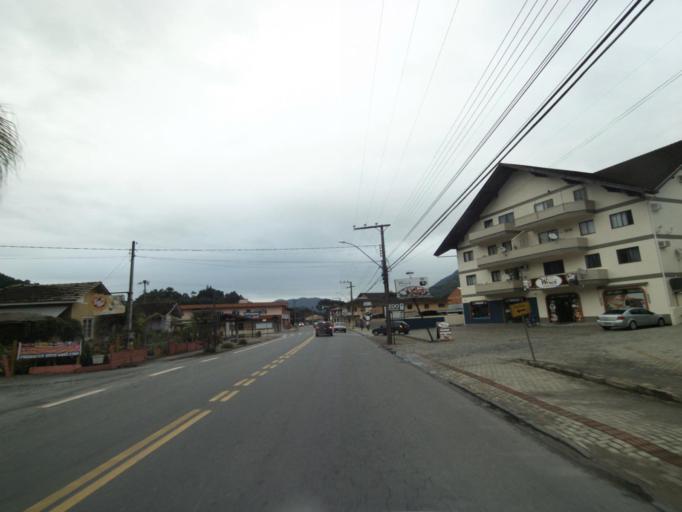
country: BR
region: Santa Catarina
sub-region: Pomerode
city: Pomerode
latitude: -26.7247
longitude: -49.1703
